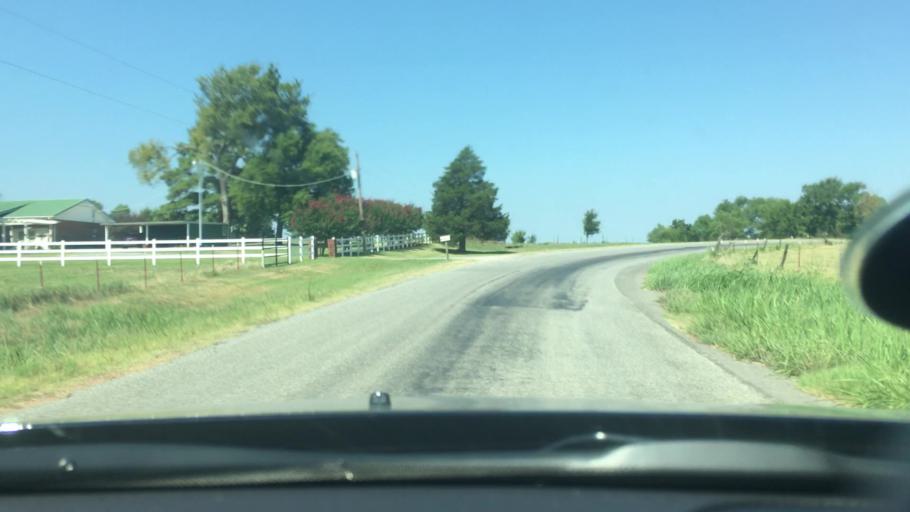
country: US
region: Oklahoma
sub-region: Johnston County
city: Tishomingo
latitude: 34.3104
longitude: -96.6347
